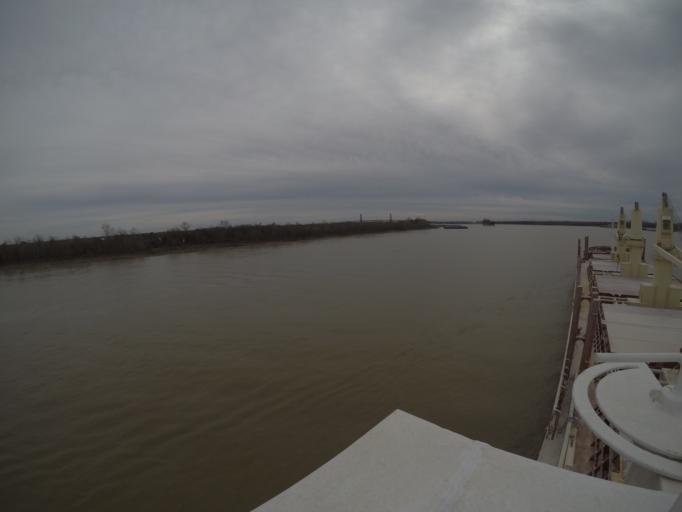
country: US
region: Louisiana
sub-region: Saint Charles Parish
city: New Sarpy
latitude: 29.9655
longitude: -90.3953
